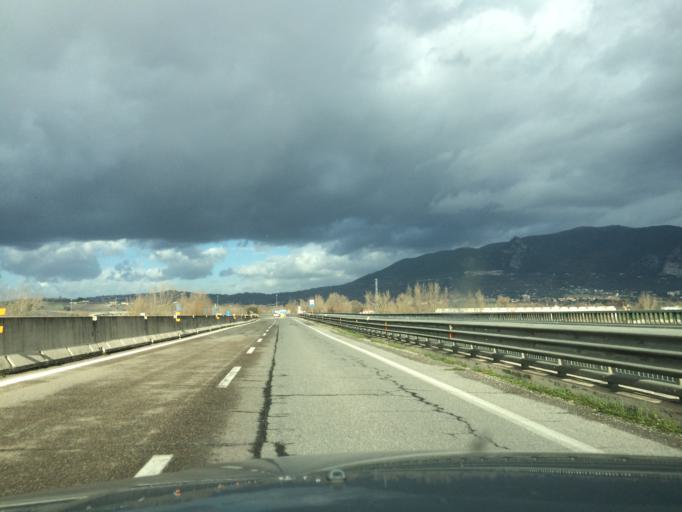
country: IT
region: Umbria
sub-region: Provincia di Terni
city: Terni
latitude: 42.5601
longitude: 12.5820
